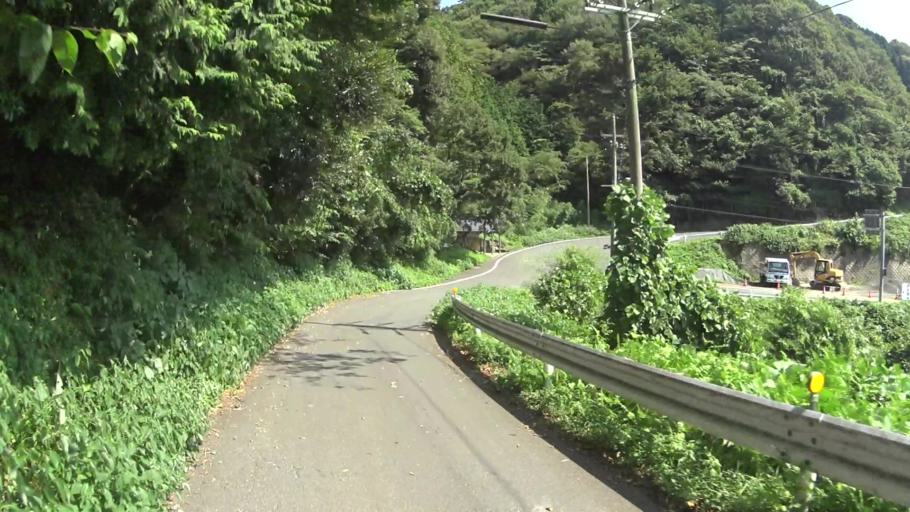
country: JP
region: Kyoto
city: Miyazu
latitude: 35.6754
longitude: 135.2432
